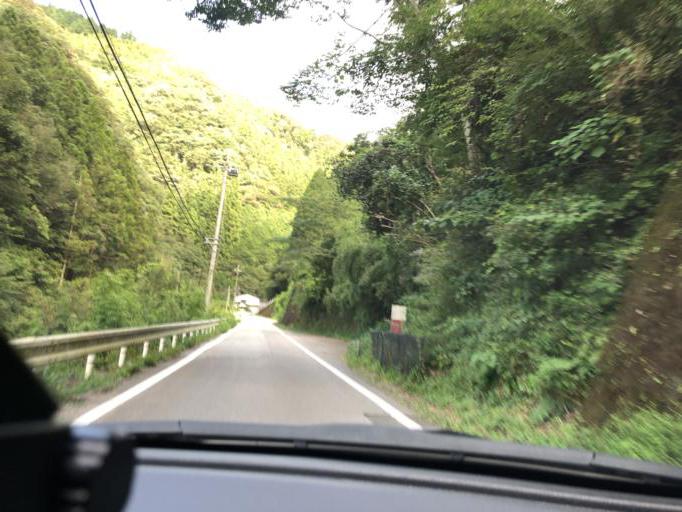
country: JP
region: Kochi
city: Kochi-shi
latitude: 33.6135
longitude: 133.4984
